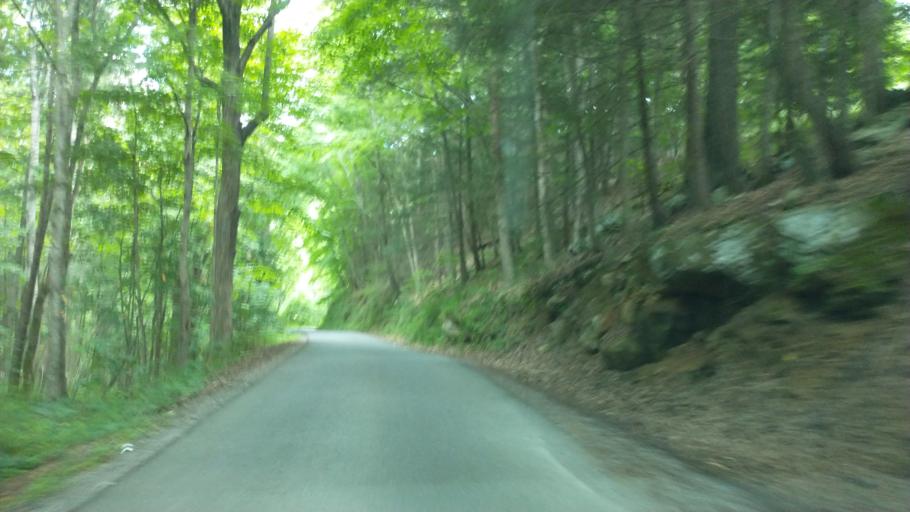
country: US
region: West Virginia
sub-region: Mercer County
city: Athens
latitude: 37.4673
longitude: -81.0635
